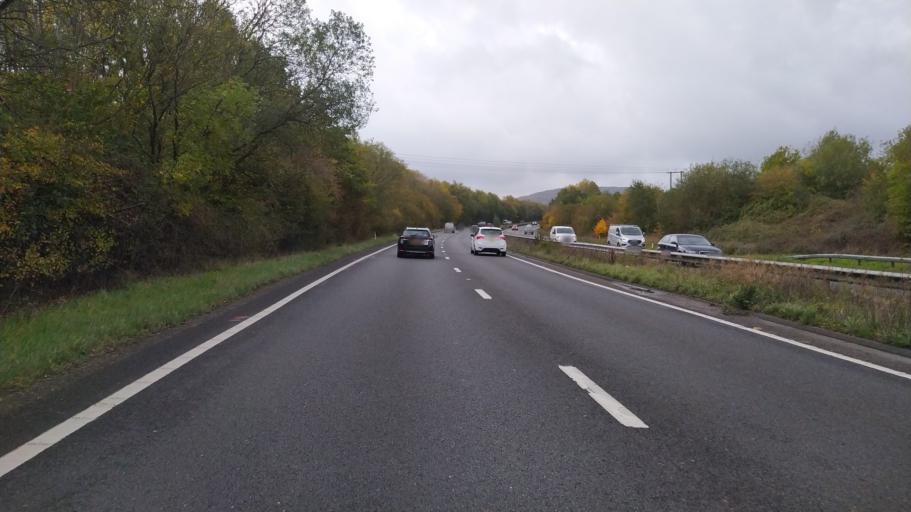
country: GB
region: England
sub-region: Hampshire
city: Petersfield
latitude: 50.9985
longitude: -0.9516
